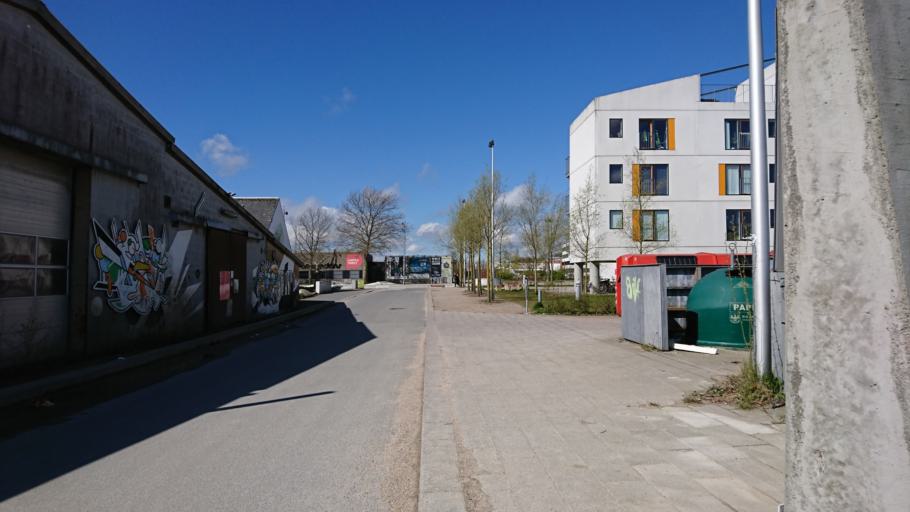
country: DK
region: Zealand
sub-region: Roskilde Kommune
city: Roskilde
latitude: 55.6290
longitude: 12.0857
